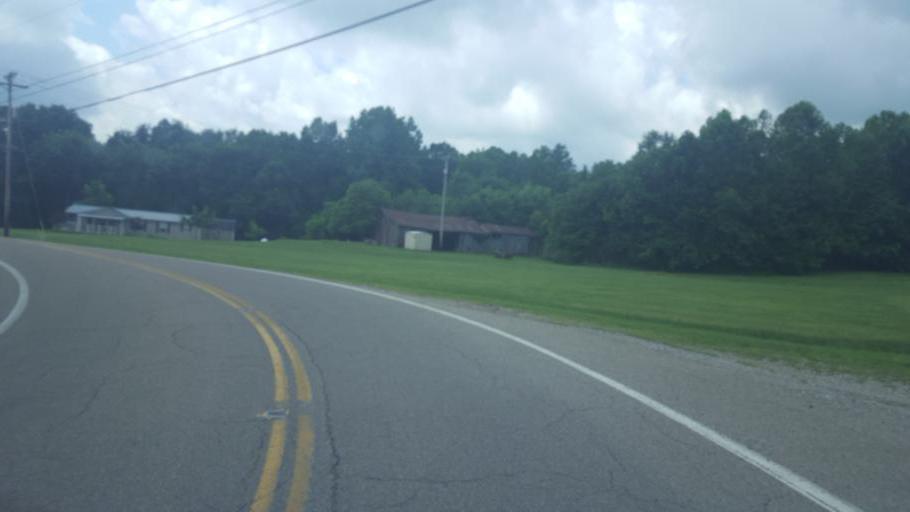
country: US
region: Ohio
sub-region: Ross County
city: Kingston
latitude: 39.4608
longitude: -82.7506
